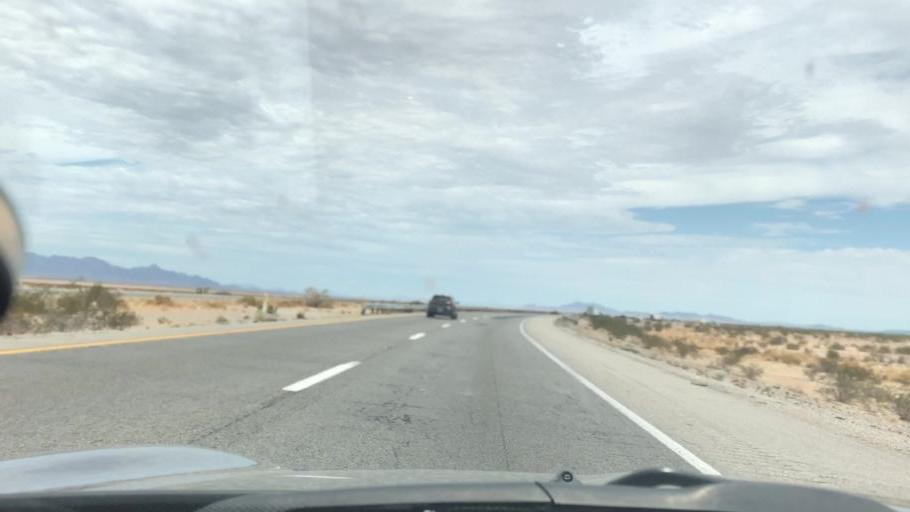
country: US
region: California
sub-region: Riverside County
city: Mesa Verde
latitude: 33.6363
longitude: -115.0842
